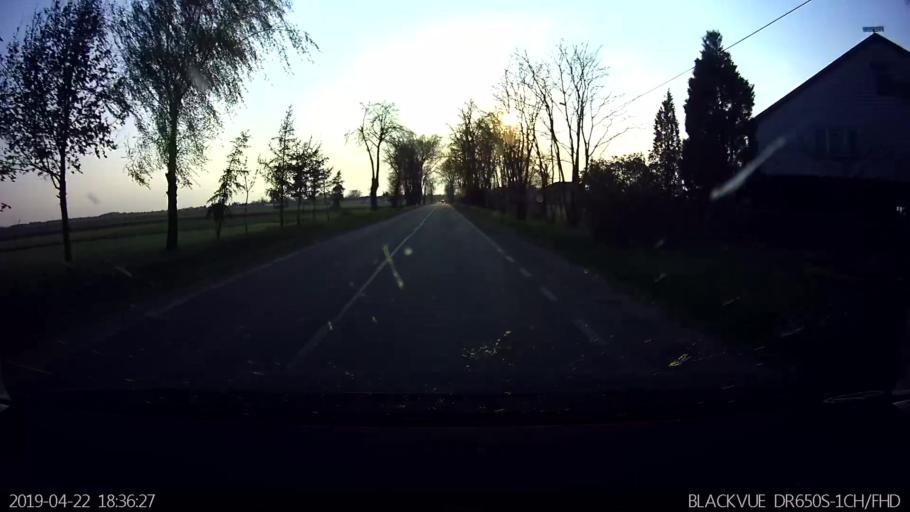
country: PL
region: Masovian Voivodeship
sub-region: Powiat wolominski
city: Klembow
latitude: 52.4456
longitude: 21.3257
